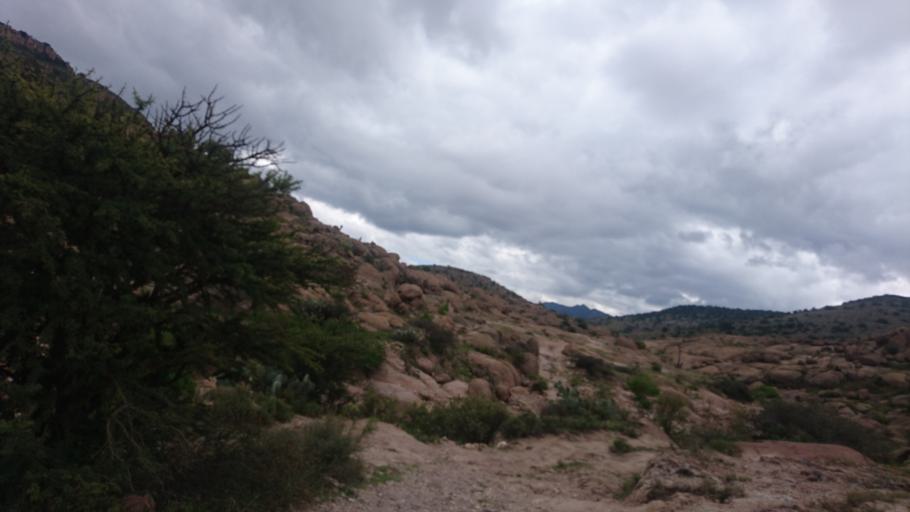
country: MX
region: San Luis Potosi
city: Escalerillas
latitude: 22.0732
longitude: -101.0938
